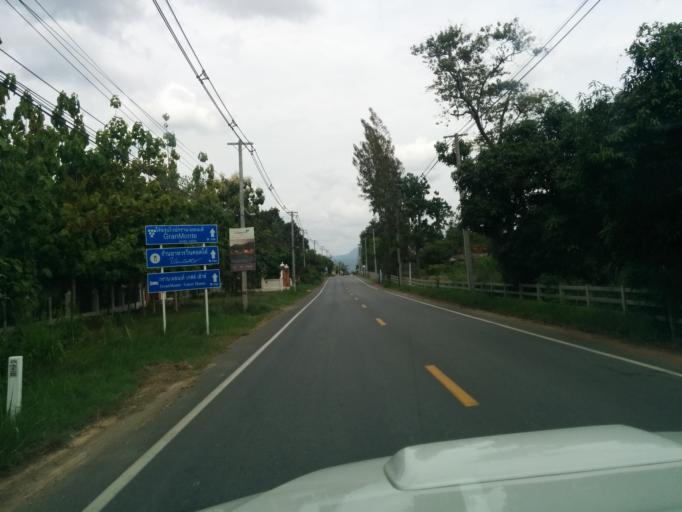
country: TH
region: Sara Buri
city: Muak Lek
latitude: 14.5945
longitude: 101.2187
